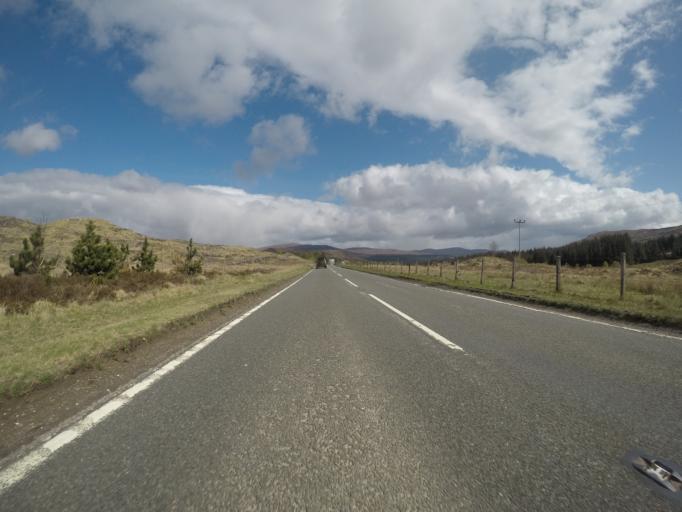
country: GB
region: Scotland
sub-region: Highland
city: Spean Bridge
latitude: 57.1384
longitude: -4.9537
